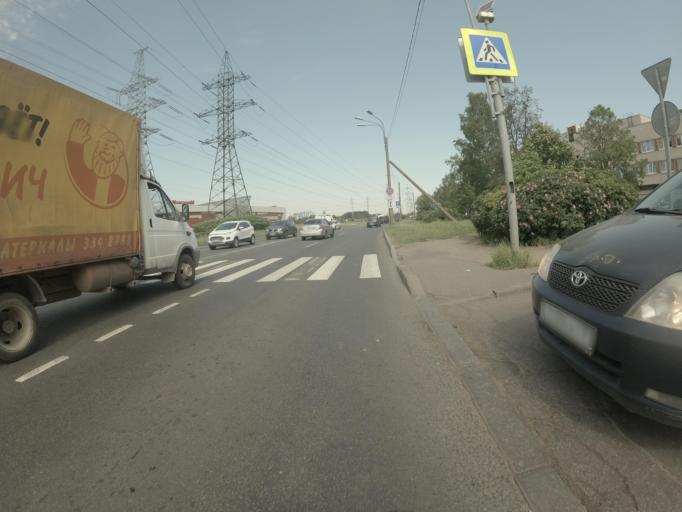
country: RU
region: St.-Petersburg
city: Krasnogvargeisky
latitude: 59.9458
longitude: 30.4614
